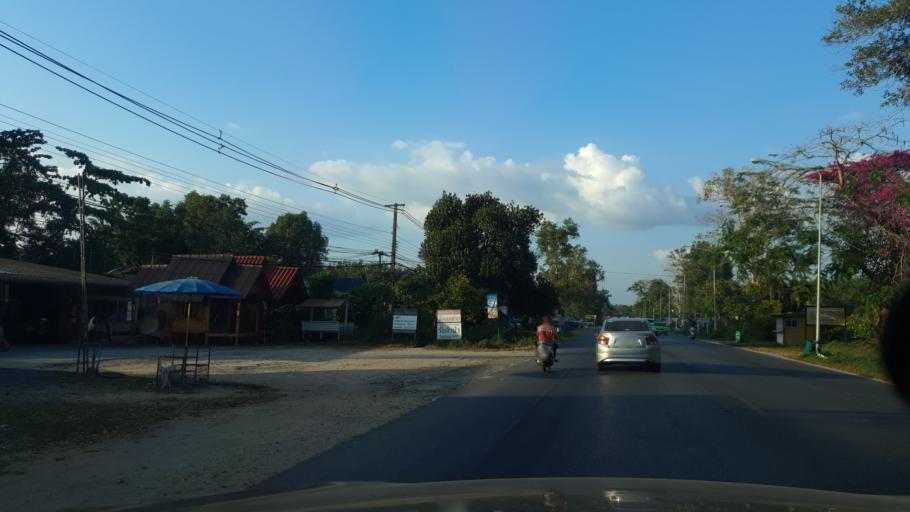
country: TH
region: Phangnga
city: Takua Pa
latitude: 8.8338
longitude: 98.2835
